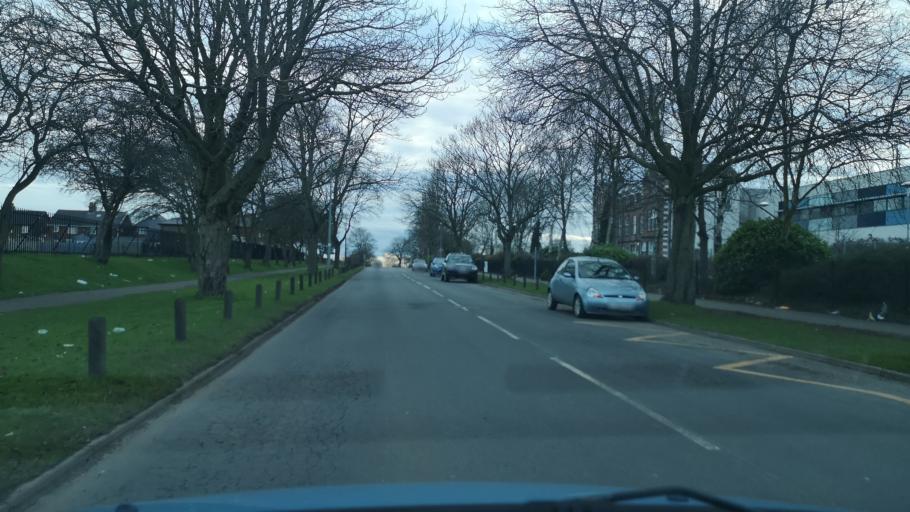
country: GB
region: England
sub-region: North Lincolnshire
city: Scunthorpe
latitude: 53.5904
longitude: -0.6639
